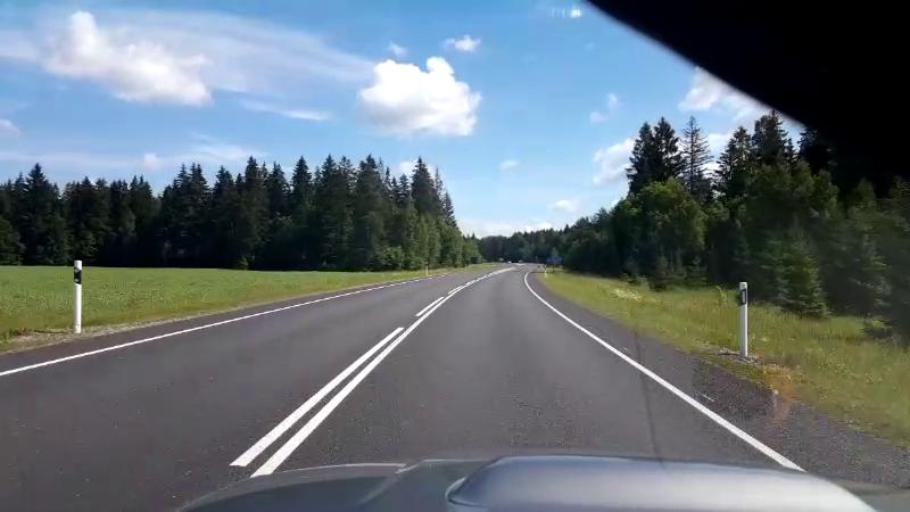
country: EE
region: Jaervamaa
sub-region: Jaerva-Jaani vald
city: Jarva-Jaani
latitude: 59.1265
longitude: 25.7425
